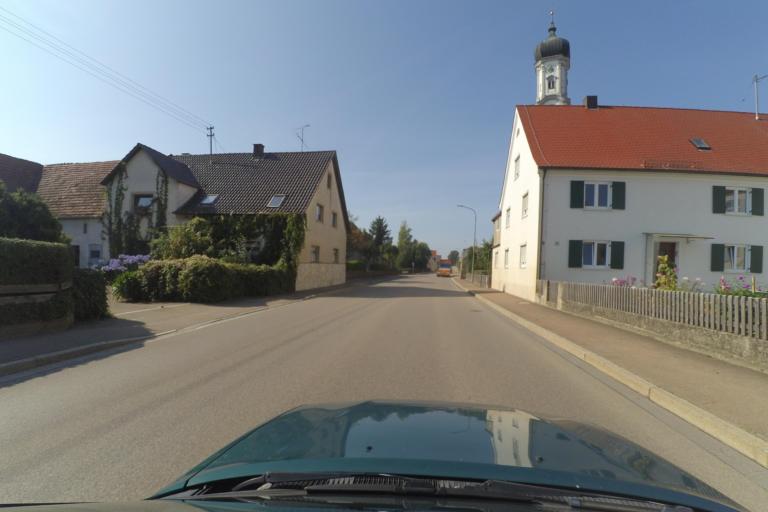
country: DE
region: Bavaria
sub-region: Swabia
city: Tapfheim
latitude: 48.6716
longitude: 10.6798
